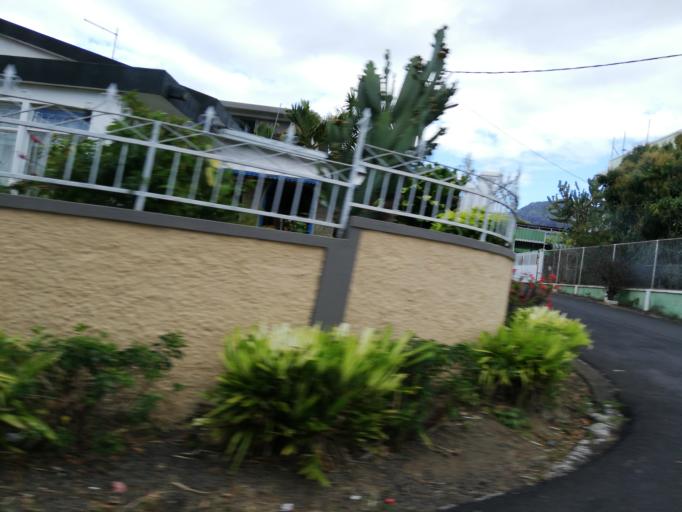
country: MU
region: Plaines Wilhems
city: Ebene
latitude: -20.2361
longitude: 57.4582
